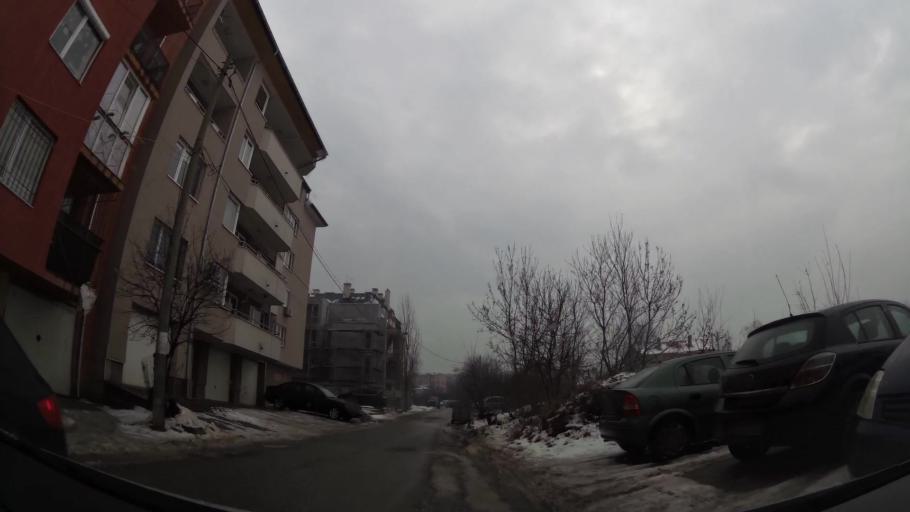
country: BG
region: Sofia-Capital
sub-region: Stolichna Obshtina
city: Sofia
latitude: 42.6805
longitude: 23.2589
